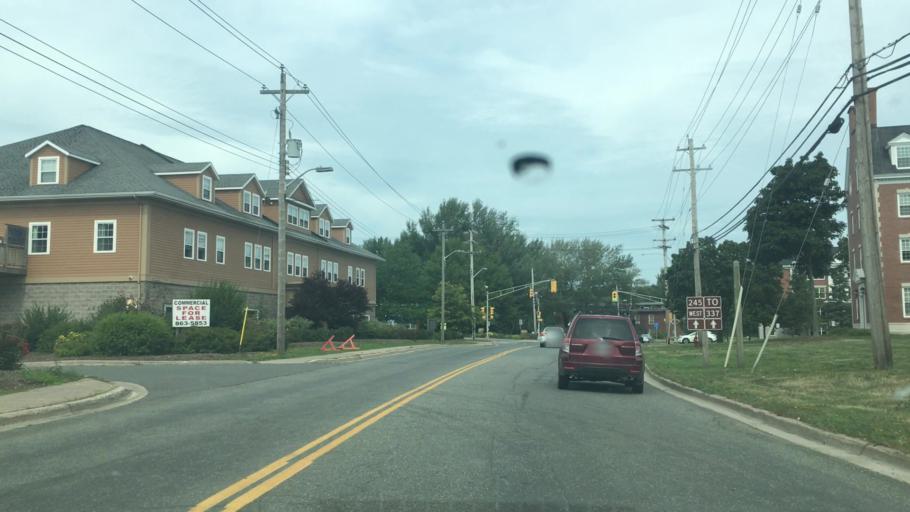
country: CA
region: Nova Scotia
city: Antigonish
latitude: 45.6155
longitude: -61.9988
